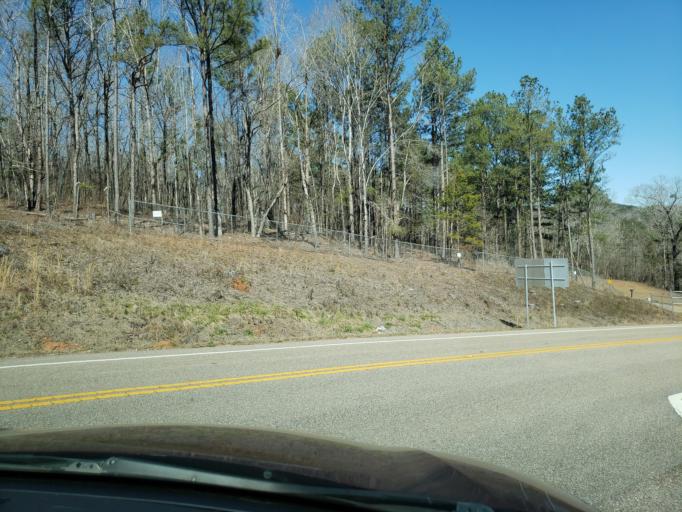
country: US
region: Alabama
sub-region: Elmore County
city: Eclectic
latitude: 32.6745
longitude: -85.9120
